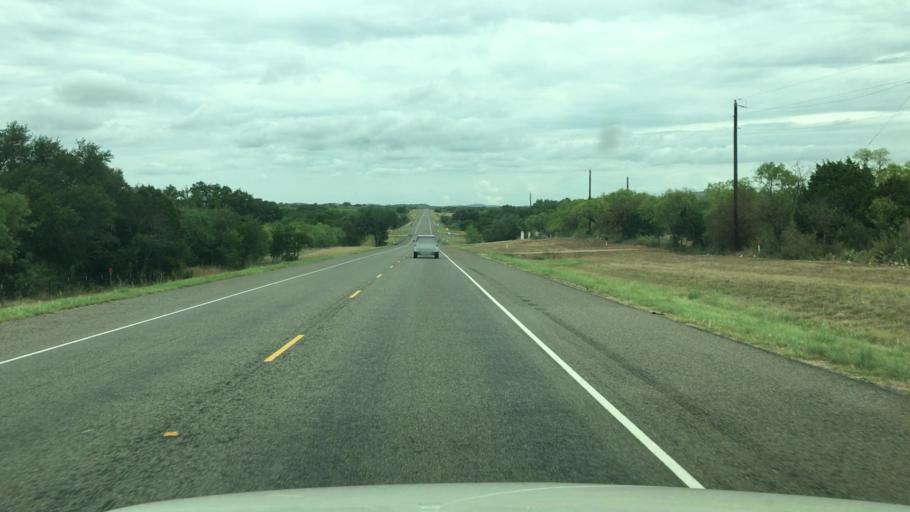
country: US
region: Texas
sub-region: Burnet County
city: Granite Shoals
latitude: 30.5539
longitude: -98.4680
